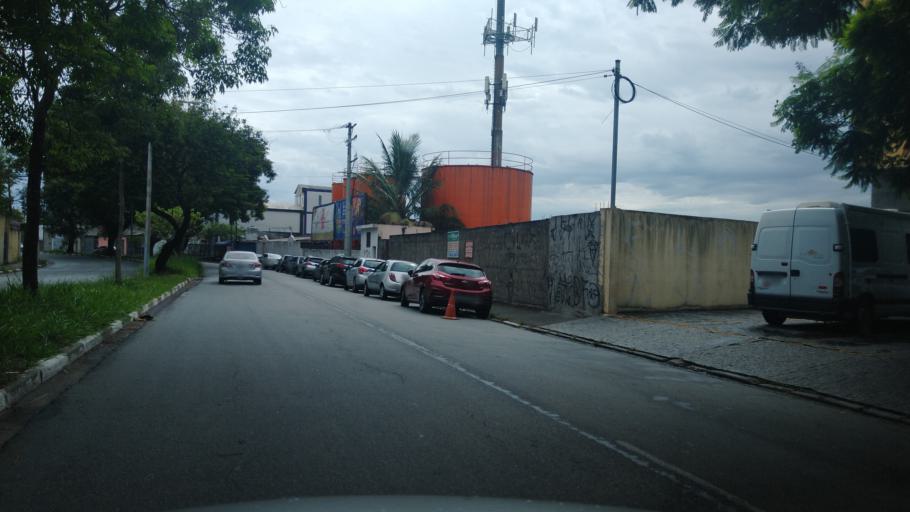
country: BR
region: Sao Paulo
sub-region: Guarulhos
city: Guarulhos
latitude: -23.4807
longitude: -46.5378
